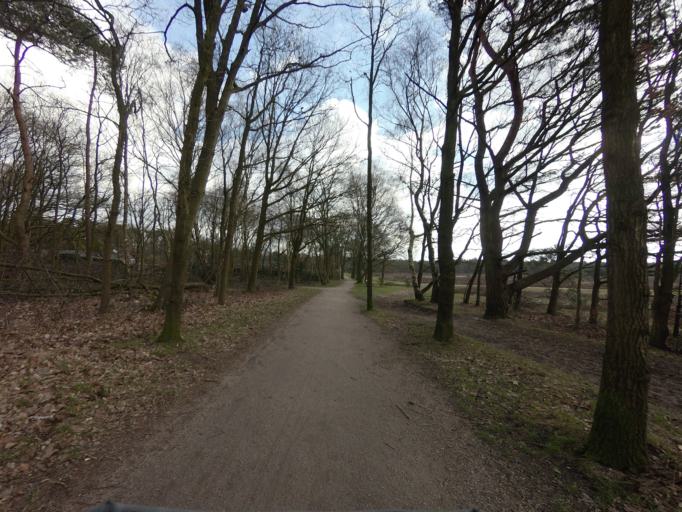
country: NL
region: North Holland
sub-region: Gemeente Hilversum
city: Hilversum
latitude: 52.2027
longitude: 5.1719
